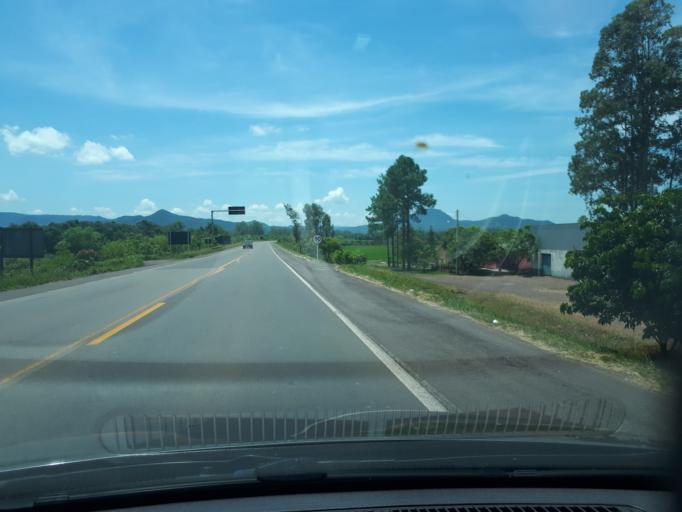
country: BR
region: Rio Grande do Sul
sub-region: Candelaria
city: Candelaria
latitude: -29.7312
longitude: -52.9448
